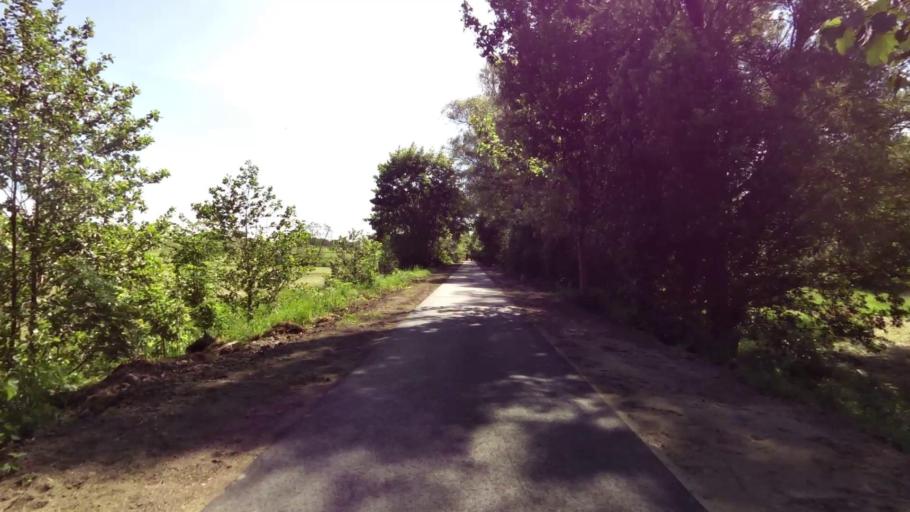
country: PL
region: West Pomeranian Voivodeship
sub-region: Powiat gryfinski
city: Gryfino
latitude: 53.2243
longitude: 14.5485
